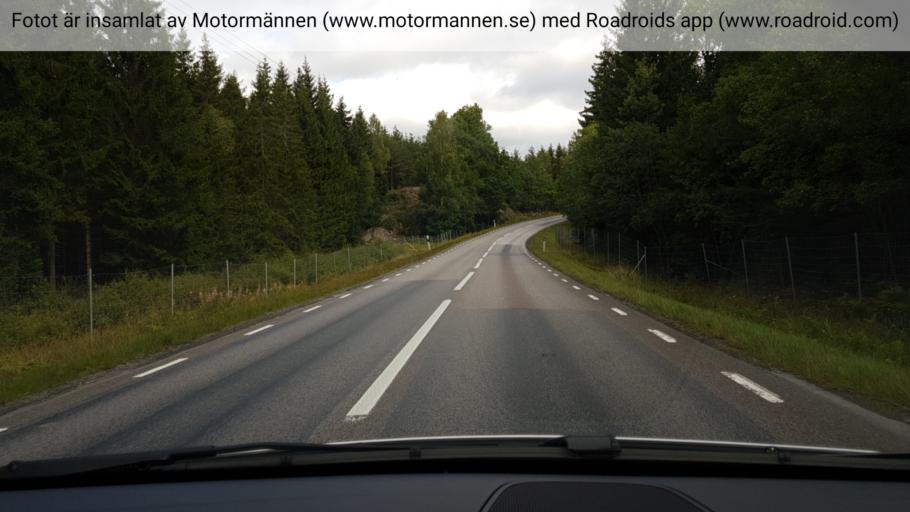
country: SE
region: Vaestra Goetaland
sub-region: Alingsas Kommun
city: Sollebrunn
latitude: 58.1868
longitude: 12.4255
